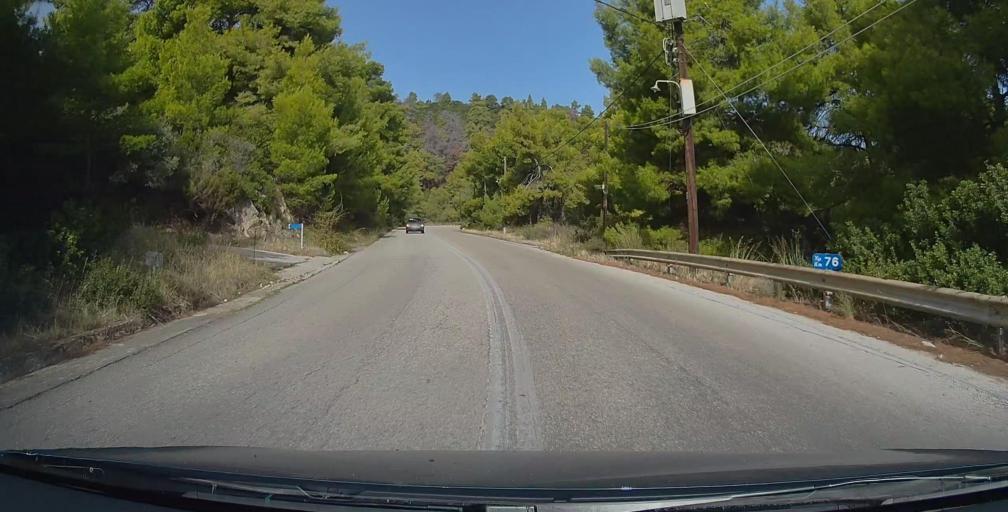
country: GR
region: Central Macedonia
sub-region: Nomos Chalkidikis
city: Sarti
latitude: 40.1087
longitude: 23.9856
